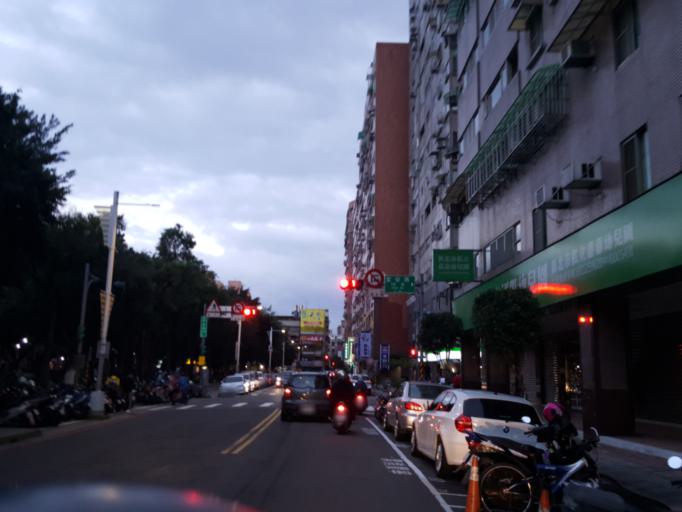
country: TW
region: Taipei
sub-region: Taipei
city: Banqiao
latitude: 24.9996
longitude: 121.5110
